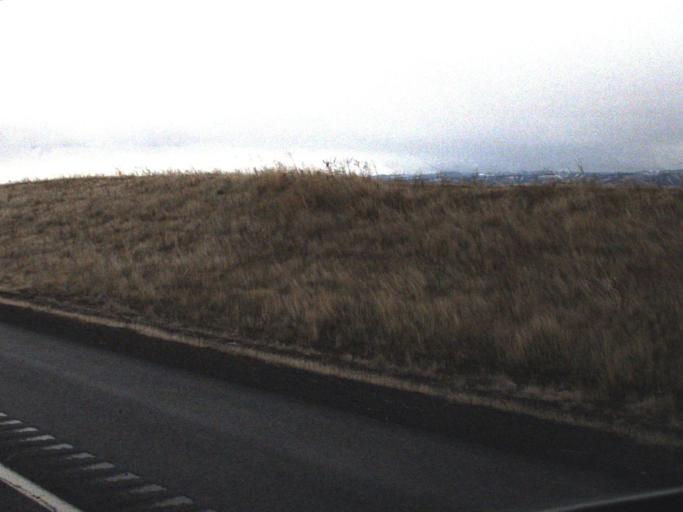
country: US
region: Washington
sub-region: Walla Walla County
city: Garrett
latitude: 46.0649
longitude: -118.4264
